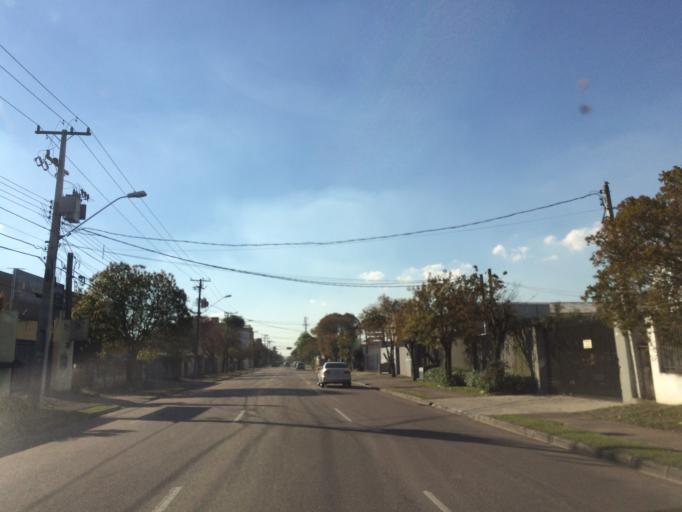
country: BR
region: Parana
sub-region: Sao Jose Dos Pinhais
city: Sao Jose dos Pinhais
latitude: -25.4894
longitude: -49.2422
